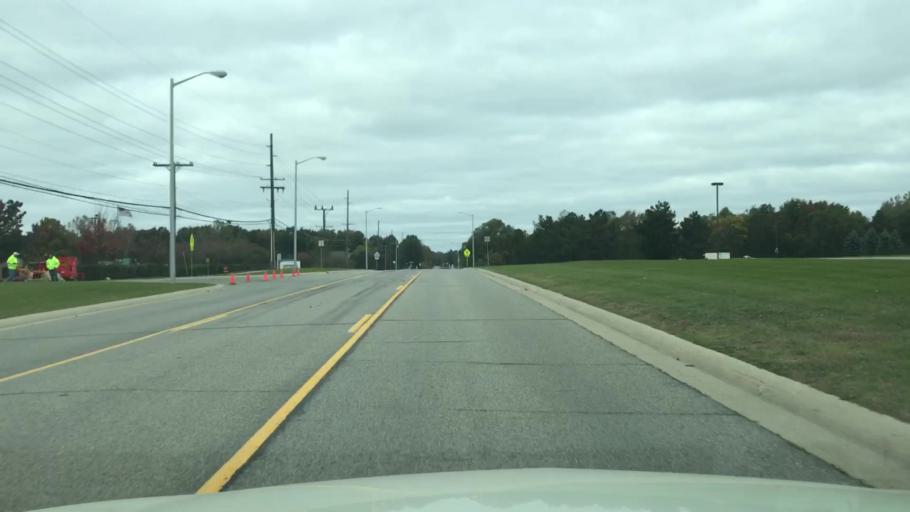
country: US
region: Michigan
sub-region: Oakland County
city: Rochester
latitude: 42.6995
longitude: -83.1237
